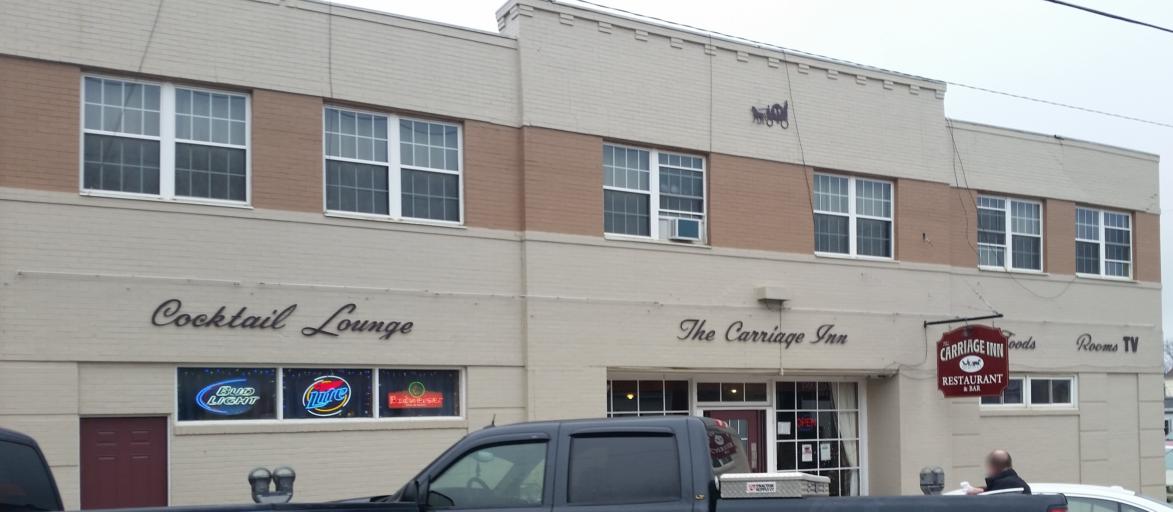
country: US
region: Pennsylvania
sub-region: Clarion County
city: Knox
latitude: 41.2346
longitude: -79.5361
